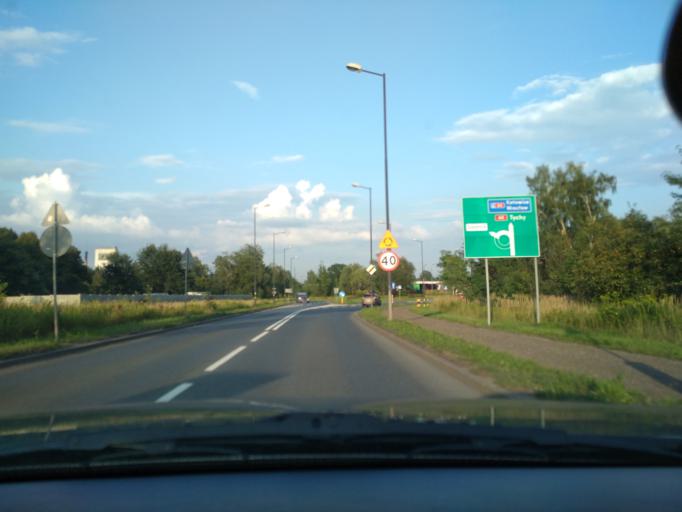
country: PL
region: Silesian Voivodeship
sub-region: Gliwice
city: Gliwice
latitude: 50.2713
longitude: 18.7000
